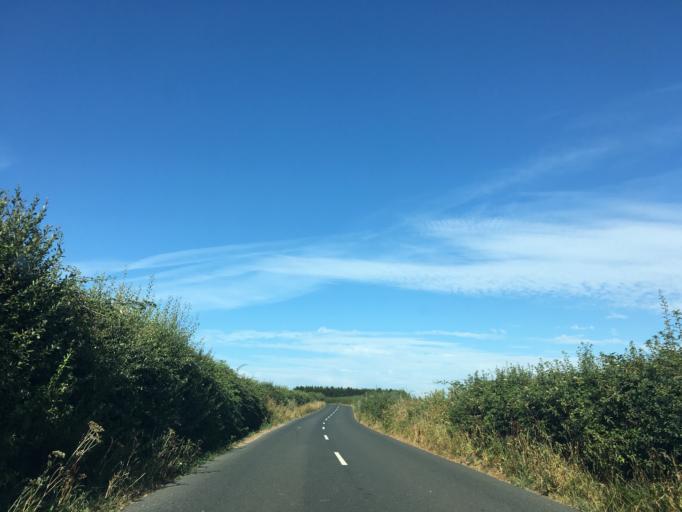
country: GB
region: England
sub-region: Isle of Wight
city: Niton
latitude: 50.6236
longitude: -1.2853
